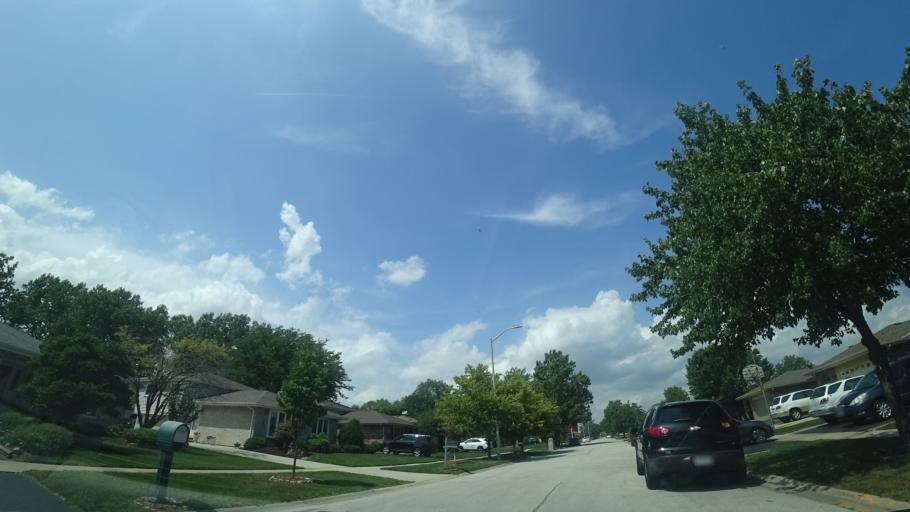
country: US
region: Illinois
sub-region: Cook County
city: Crestwood
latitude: 41.6716
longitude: -87.7517
